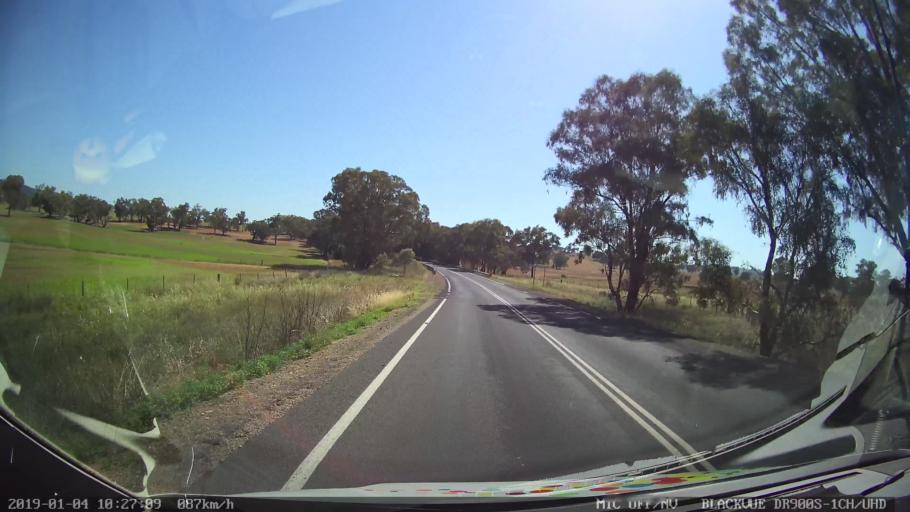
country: AU
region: New South Wales
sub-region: Cabonne
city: Canowindra
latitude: -33.3732
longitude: 148.5957
